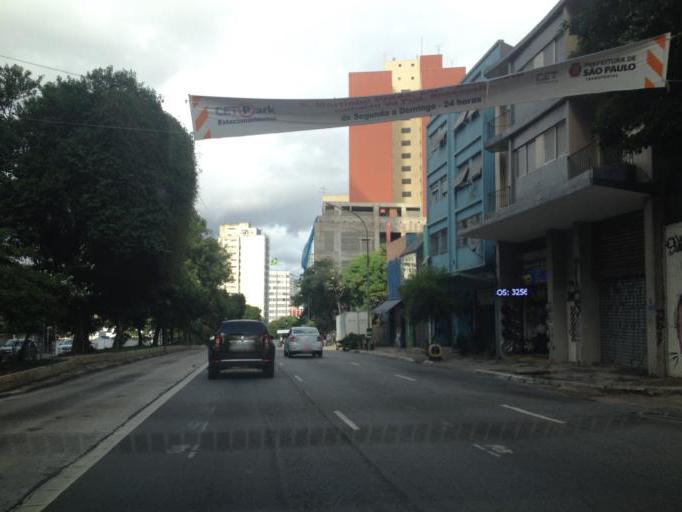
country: BR
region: Sao Paulo
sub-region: Sao Paulo
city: Sao Paulo
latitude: -23.5496
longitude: -46.6532
